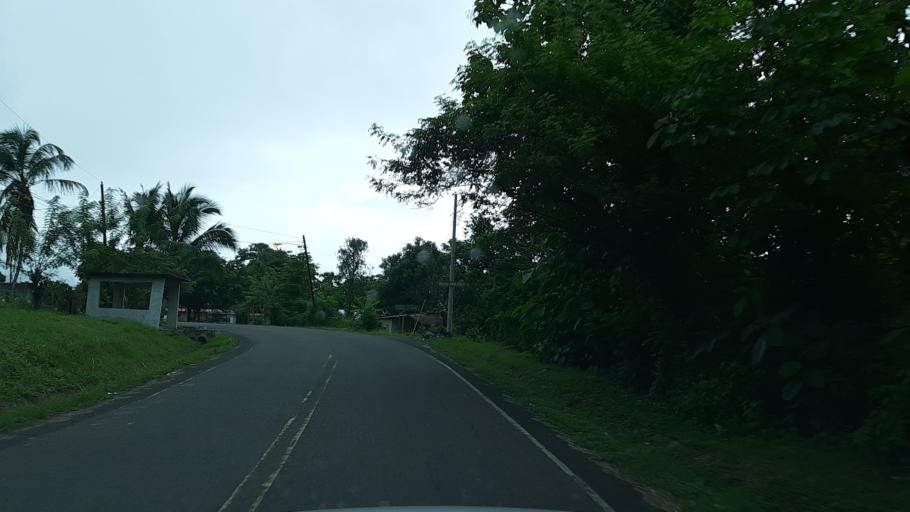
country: PA
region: Colon
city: Nuevo San Juan
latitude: 9.2422
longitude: -79.6577
